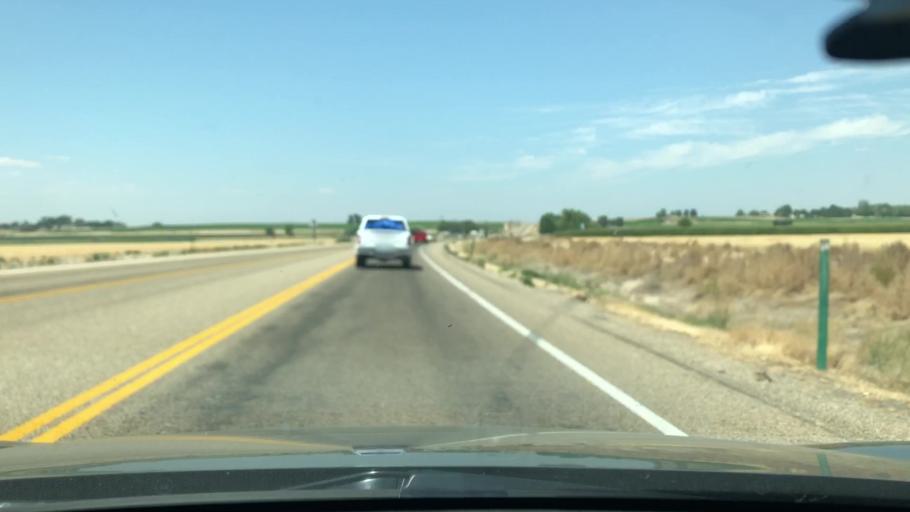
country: US
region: Idaho
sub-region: Canyon County
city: Parma
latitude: 43.8084
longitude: -116.9540
